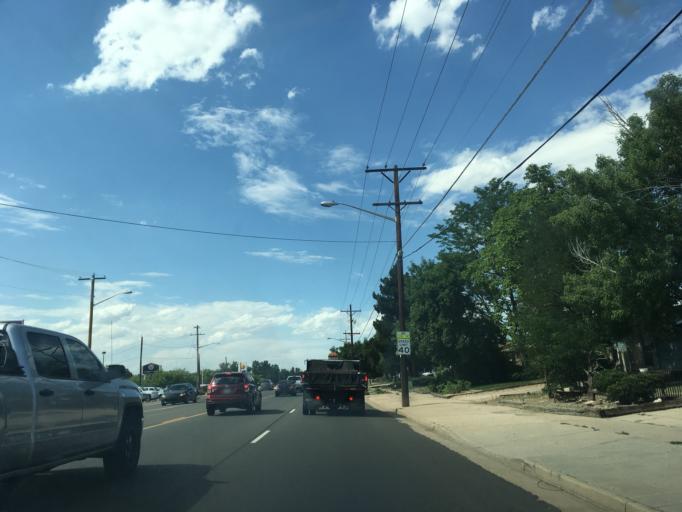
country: US
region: Colorado
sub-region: Jefferson County
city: Lakewood
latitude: 39.6799
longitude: -105.0532
